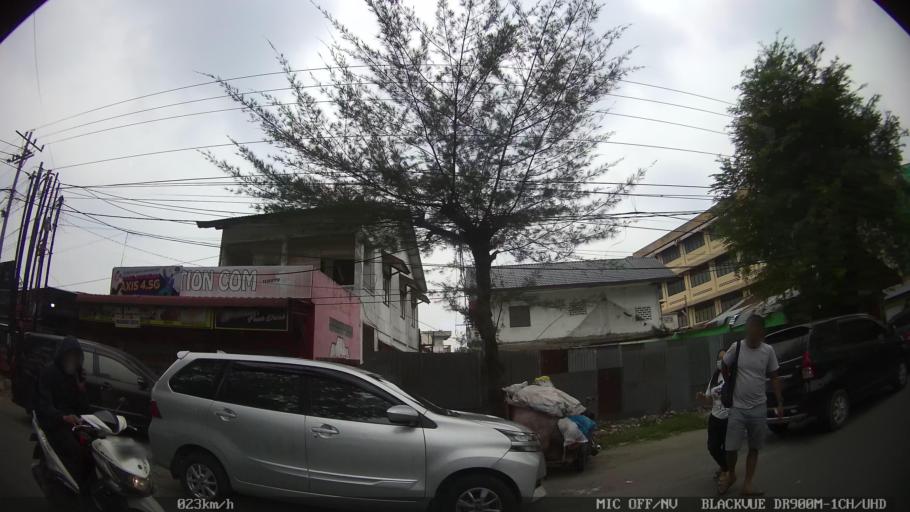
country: ID
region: North Sumatra
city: Medan
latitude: 3.5629
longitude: 98.6944
